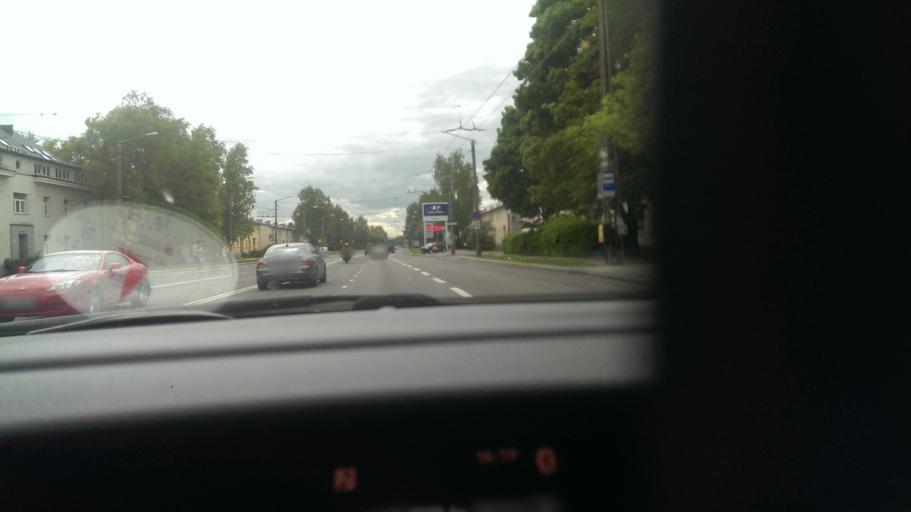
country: EE
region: Harju
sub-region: Tallinna linn
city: Tallinn
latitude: 59.4260
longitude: 24.7183
